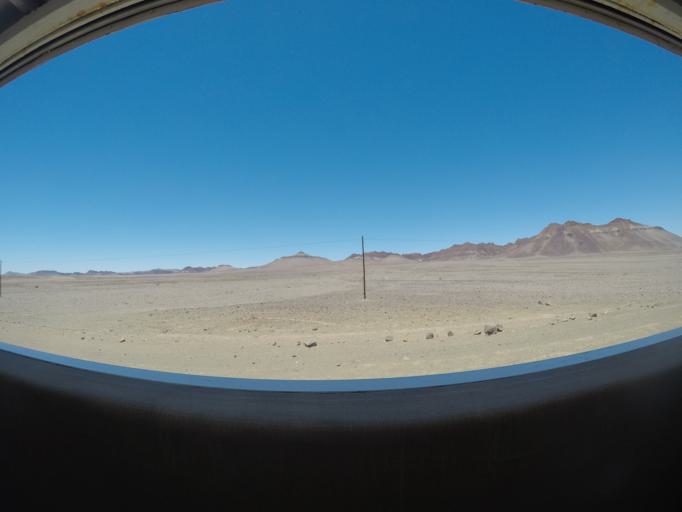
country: ZA
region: Northern Cape
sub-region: Namakwa District Municipality
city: Port Nolloth
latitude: -28.6045
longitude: 17.4866
